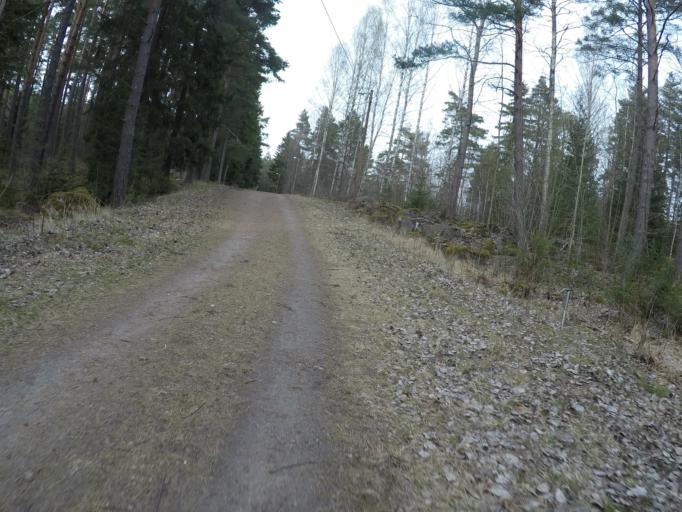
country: SE
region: Soedermanland
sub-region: Eskilstuna Kommun
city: Torshalla
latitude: 59.4233
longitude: 16.4990
